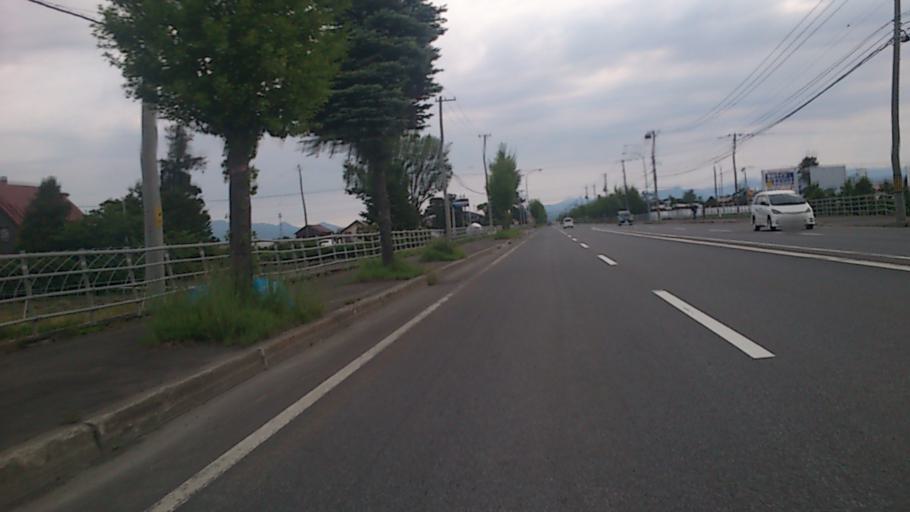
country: JP
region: Hokkaido
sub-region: Asahikawa-shi
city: Asahikawa
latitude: 43.8268
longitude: 142.4600
